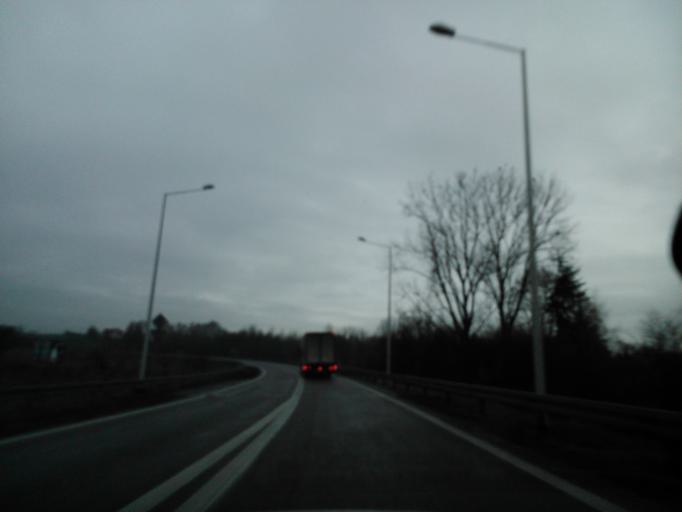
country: PL
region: Lublin Voivodeship
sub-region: Powiat krasnicki
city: Krasnik
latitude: 50.9178
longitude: 22.2367
